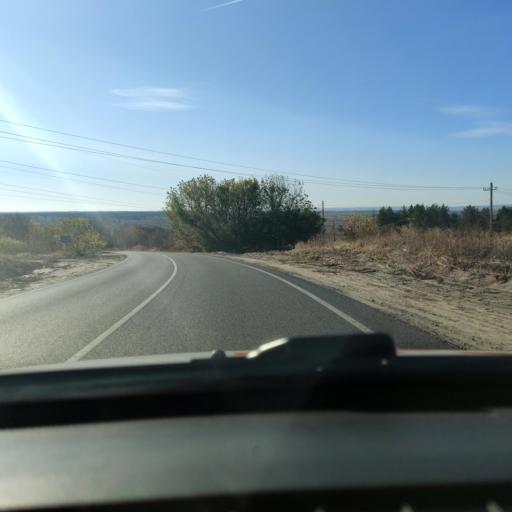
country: RU
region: Voronezj
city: Shilovo
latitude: 51.5547
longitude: 39.1326
